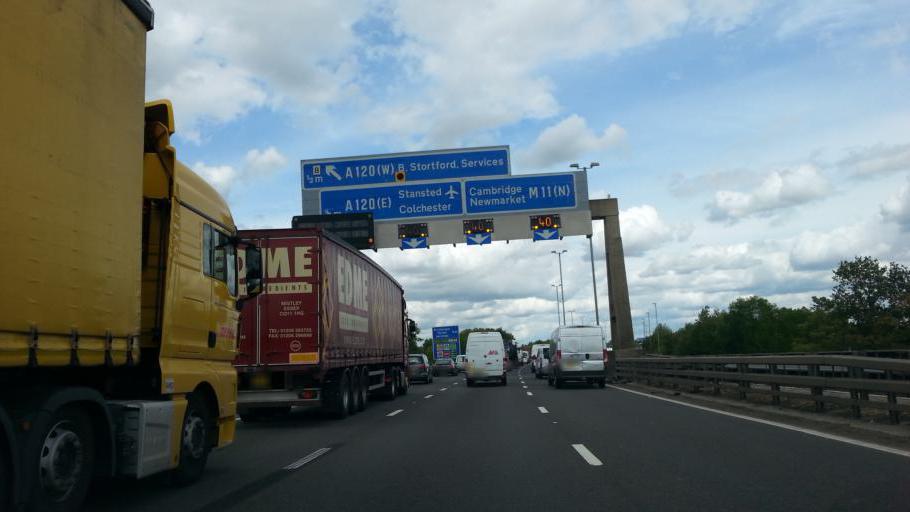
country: GB
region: England
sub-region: Essex
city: Little Hallingbury
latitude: 51.8553
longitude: 0.1854
